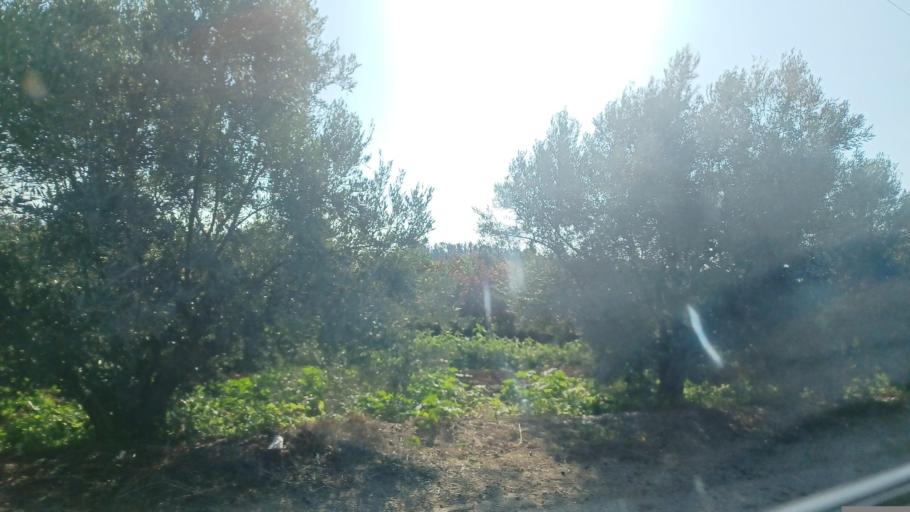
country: CY
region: Pafos
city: Paphos
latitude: 34.7216
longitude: 32.5267
